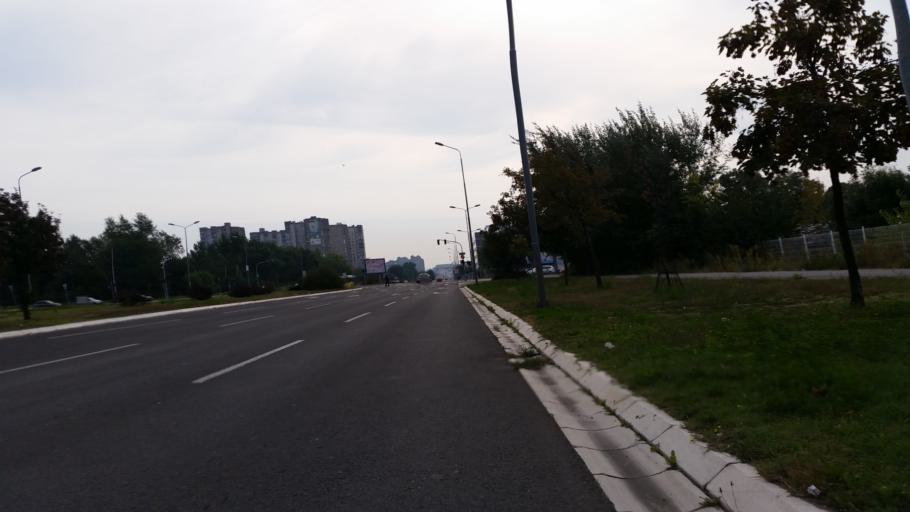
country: RS
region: Central Serbia
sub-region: Belgrade
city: Novi Beograd
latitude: 44.8154
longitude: 20.4035
